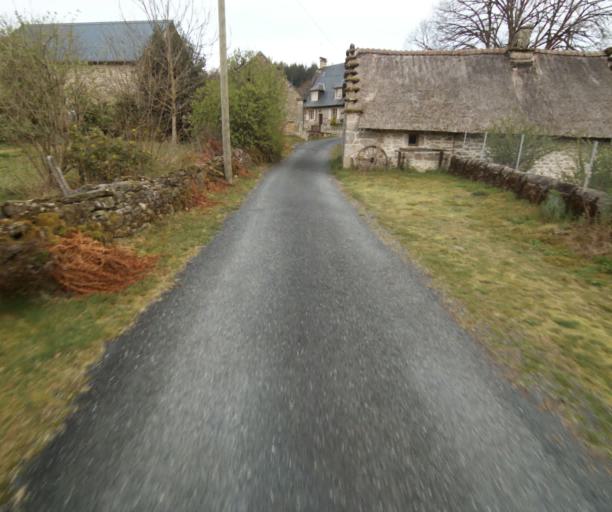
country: FR
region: Limousin
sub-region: Departement de la Correze
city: Correze
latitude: 45.4230
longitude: 1.8713
